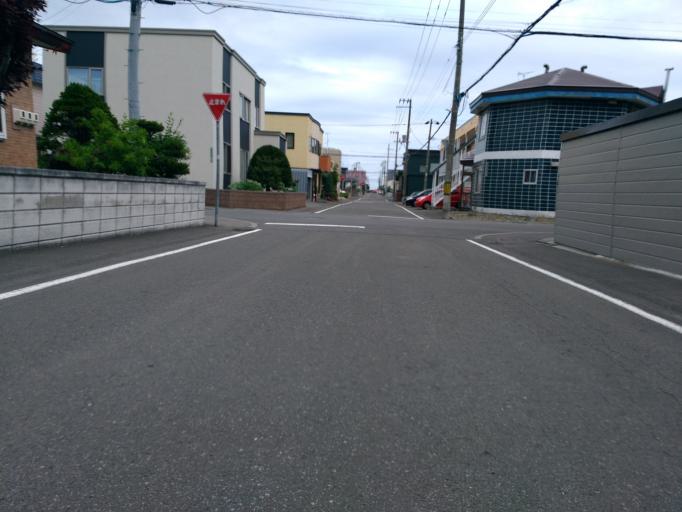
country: JP
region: Hokkaido
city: Ebetsu
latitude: 43.0853
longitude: 141.5267
